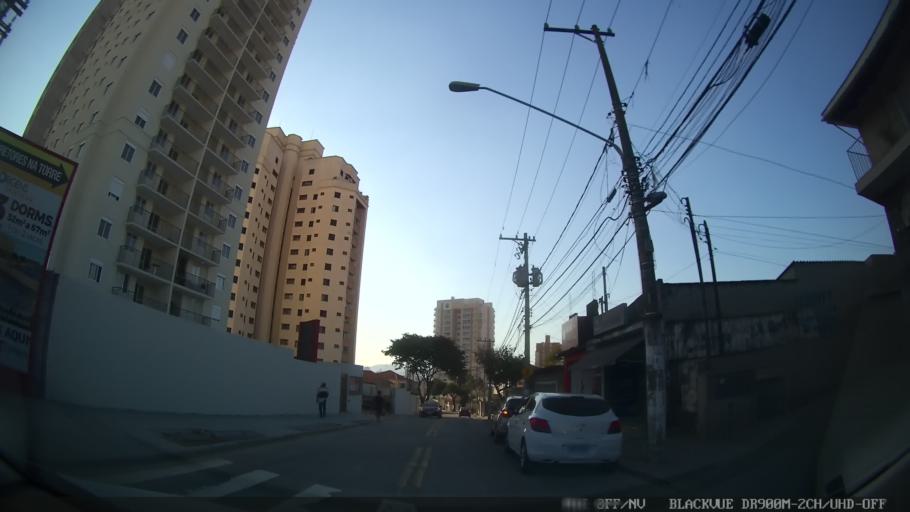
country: BR
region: Sao Paulo
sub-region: Sao Paulo
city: Sao Paulo
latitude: -23.4902
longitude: -46.6427
